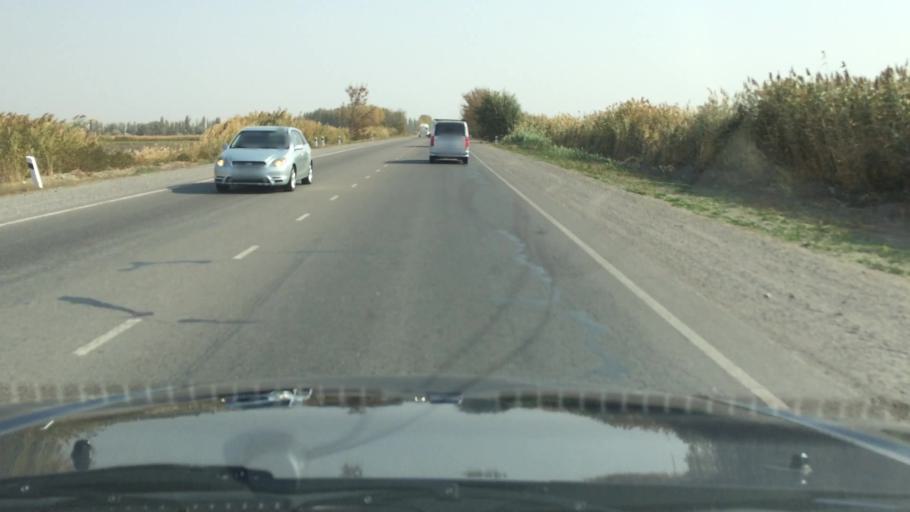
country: KG
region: Chuy
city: Lebedinovka
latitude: 42.9199
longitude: 74.7276
